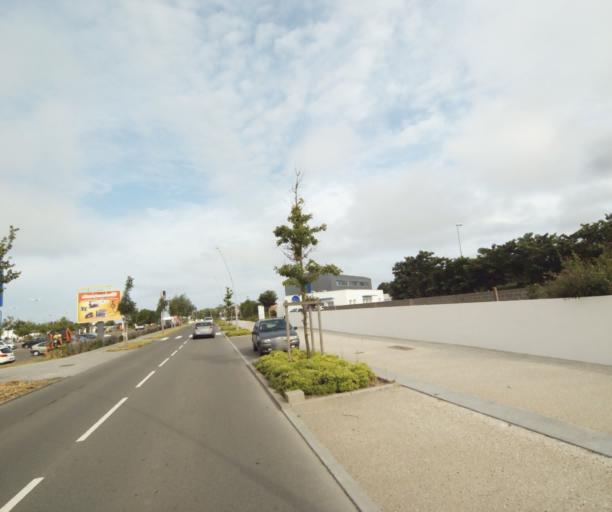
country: FR
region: Pays de la Loire
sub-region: Departement de la Vendee
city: Chateau-d'Olonne
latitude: 46.4878
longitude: -1.7446
